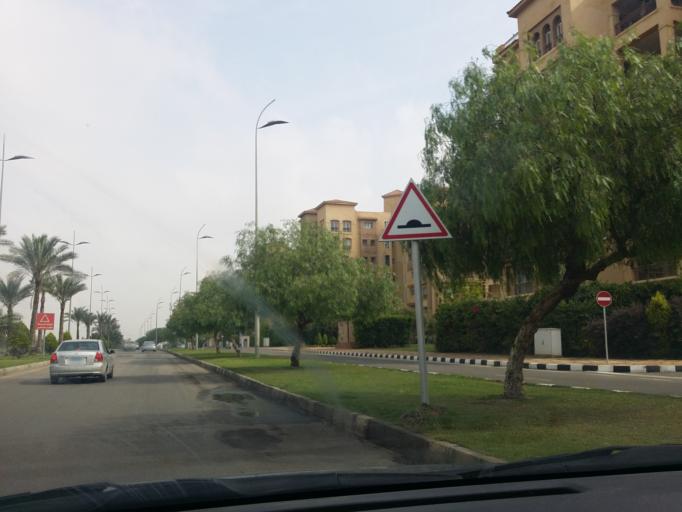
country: EG
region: Muhafazat al Qalyubiyah
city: Al Khankah
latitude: 30.1002
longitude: 31.6338
